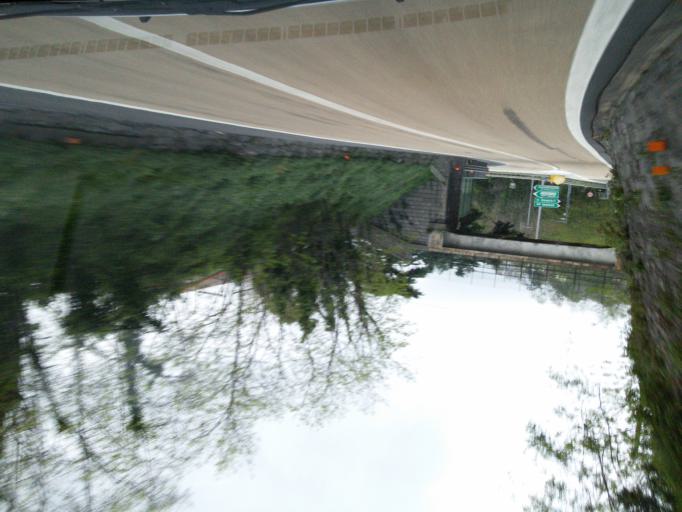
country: IT
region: Liguria
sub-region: Provincia di Genova
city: Genoa
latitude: 44.4500
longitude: 8.8959
